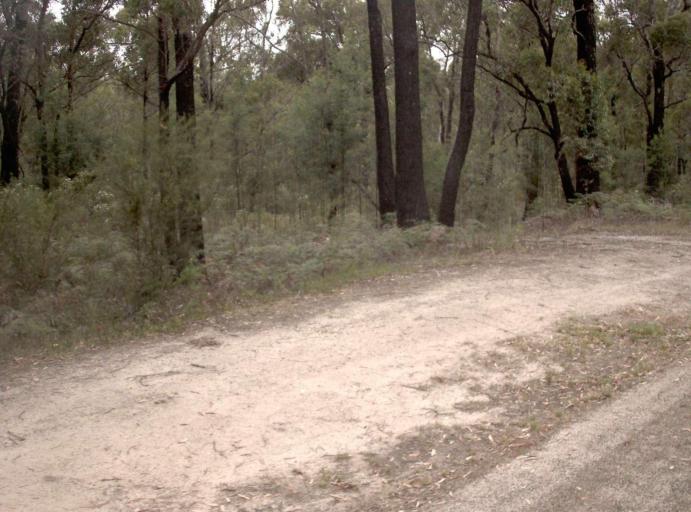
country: AU
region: Victoria
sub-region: Latrobe
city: Traralgon
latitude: -38.4714
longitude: 146.8228
